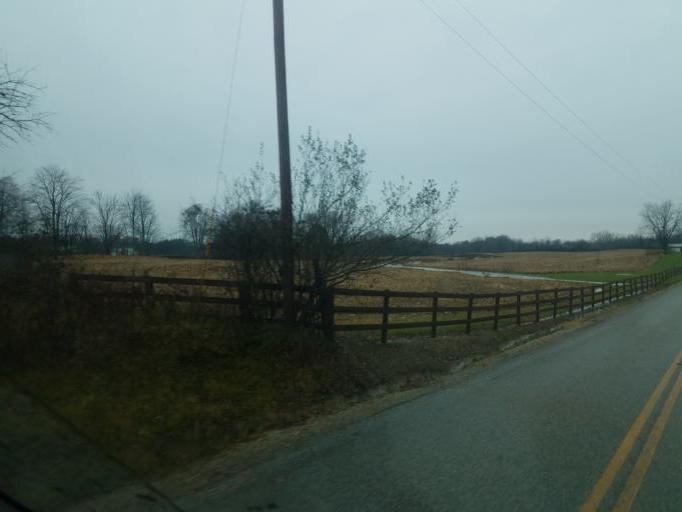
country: US
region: Ohio
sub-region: Knox County
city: Centerburg
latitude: 40.3224
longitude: -82.7709
